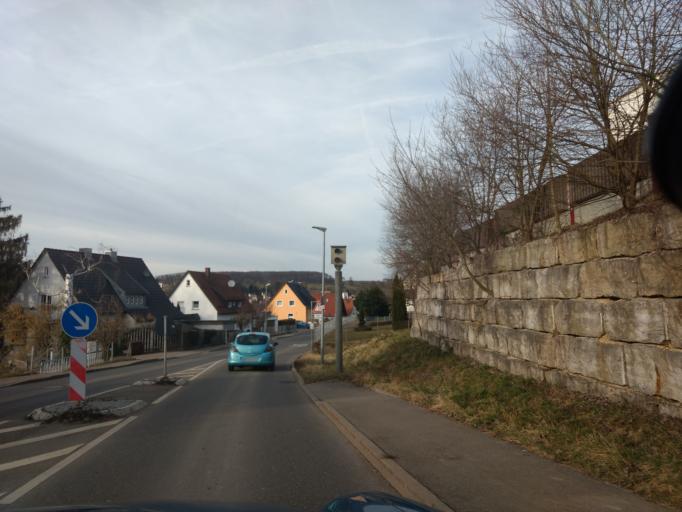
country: DE
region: Baden-Wuerttemberg
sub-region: Regierungsbezirk Stuttgart
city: Wangen
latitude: 48.7049
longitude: 9.6177
